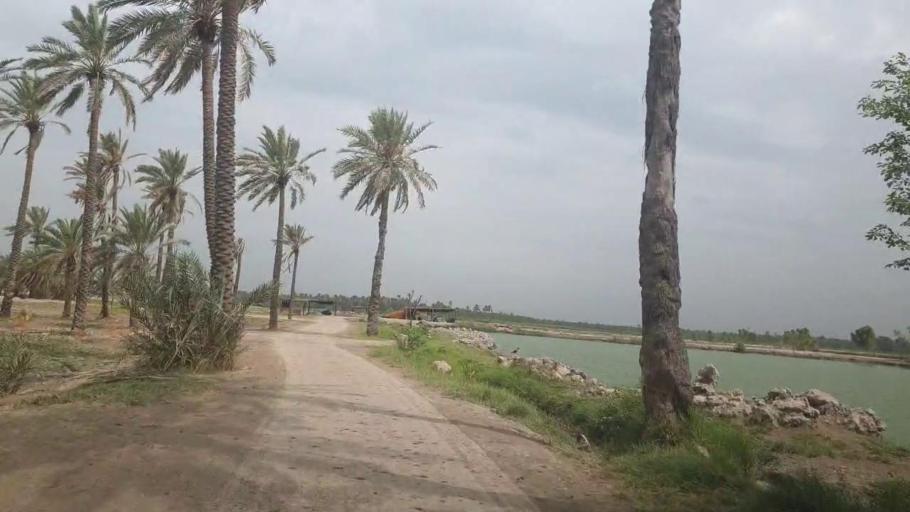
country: PK
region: Sindh
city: Khairpur
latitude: 27.5832
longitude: 68.7402
